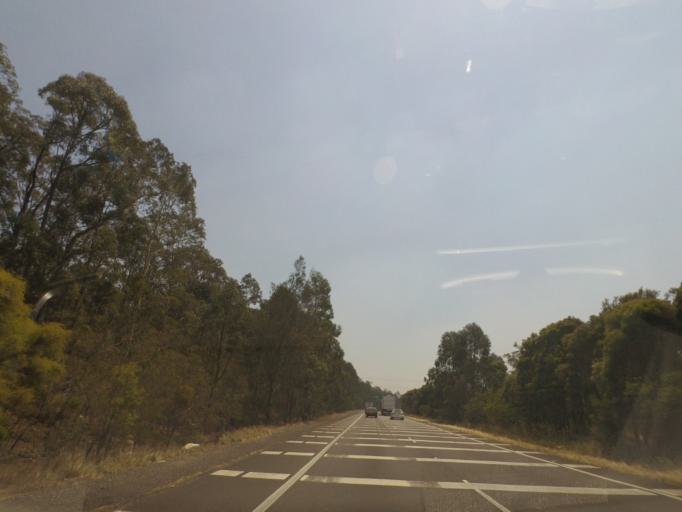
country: AU
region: New South Wales
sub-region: Newcastle
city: Beresfield
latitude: -32.8216
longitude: 151.6339
